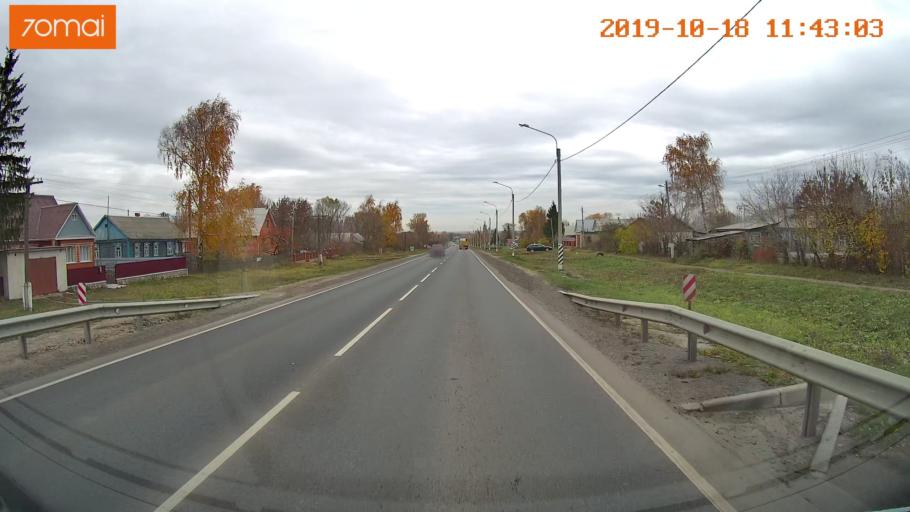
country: RU
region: Rjazan
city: Oktyabr'skiy
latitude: 54.1936
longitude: 38.9381
